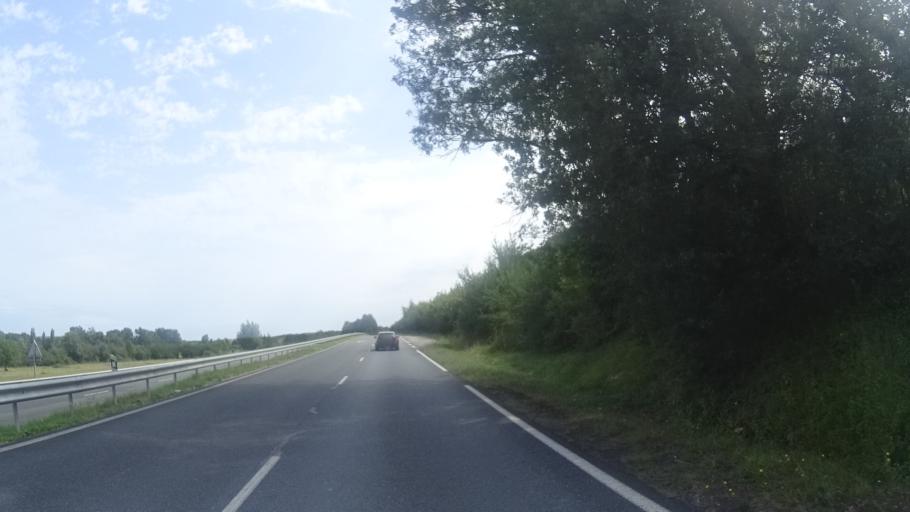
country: FR
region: Aquitaine
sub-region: Departement de la Dordogne
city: Neuvic
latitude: 45.0715
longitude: 0.4400
